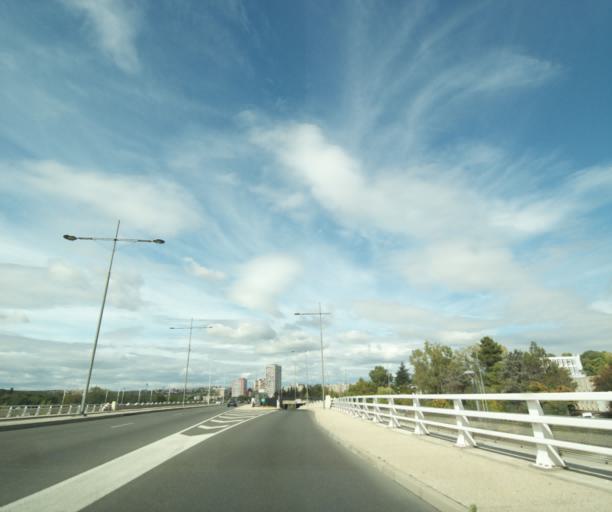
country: FR
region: Languedoc-Roussillon
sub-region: Departement de l'Herault
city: Juvignac
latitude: 43.6152
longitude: 3.8212
